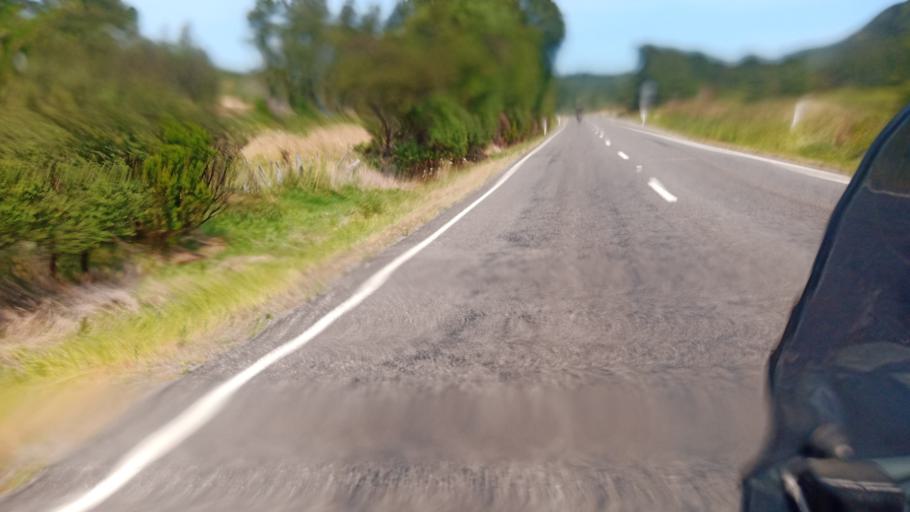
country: NZ
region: Bay of Plenty
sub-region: Opotiki District
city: Opotiki
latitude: -37.5913
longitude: 178.2197
